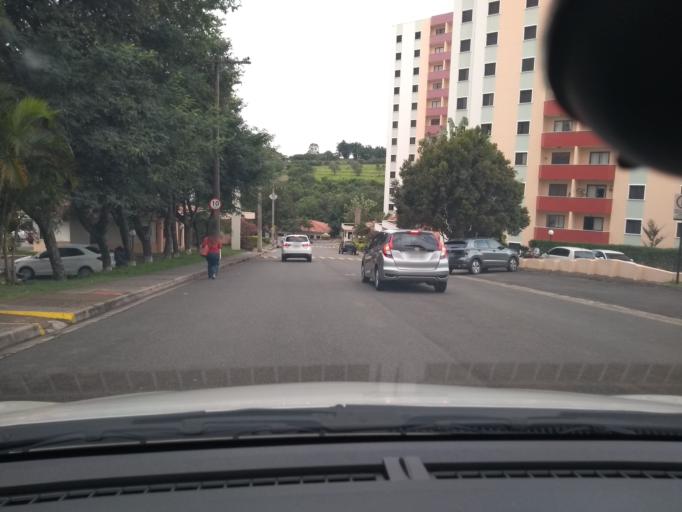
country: BR
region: Sao Paulo
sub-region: Jundiai
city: Jundiai
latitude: -23.1893
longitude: -46.9574
